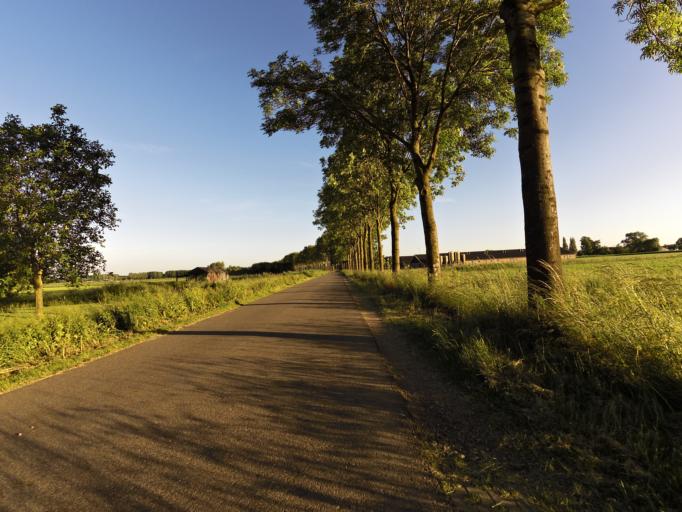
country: NL
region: Gelderland
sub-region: Gemeente Zevenaar
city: Zevenaar
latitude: 51.9518
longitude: 6.0757
